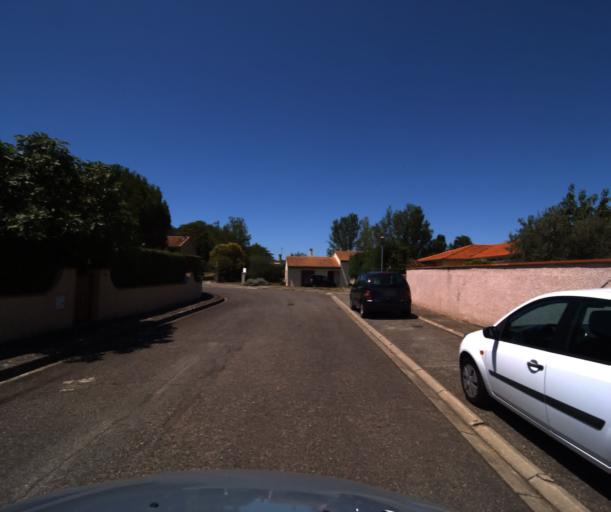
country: FR
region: Midi-Pyrenees
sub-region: Departement de la Haute-Garonne
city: Muret
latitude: 43.4583
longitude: 1.3417
